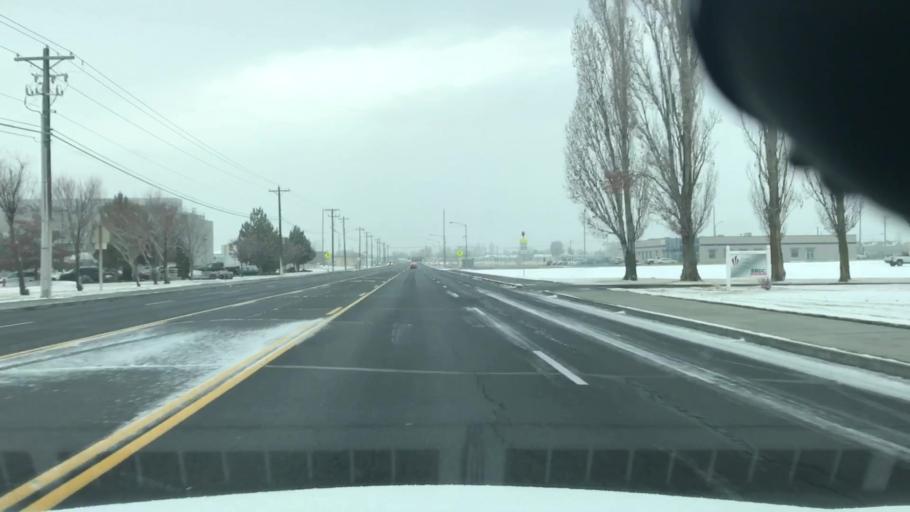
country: US
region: Washington
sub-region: Grant County
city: Moses Lake North
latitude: 47.1837
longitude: -119.3227
